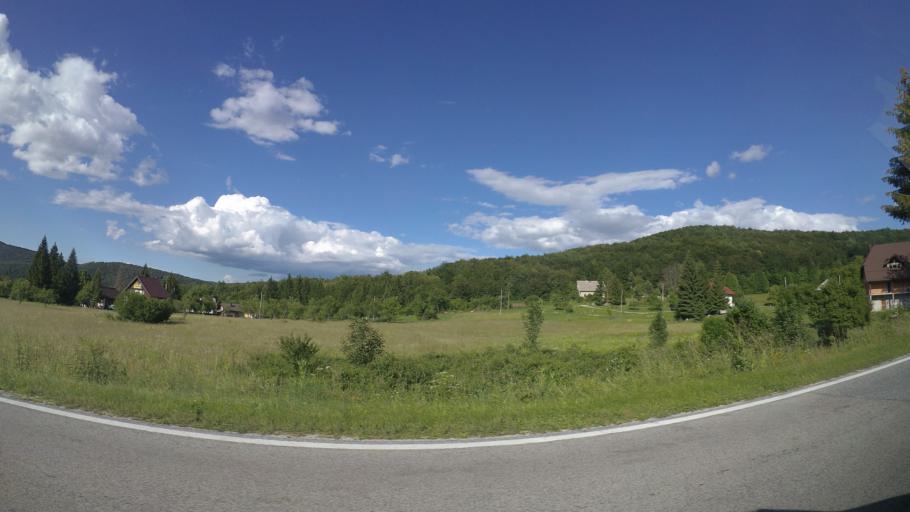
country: HR
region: Licko-Senjska
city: Jezerce
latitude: 44.8559
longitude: 15.6495
